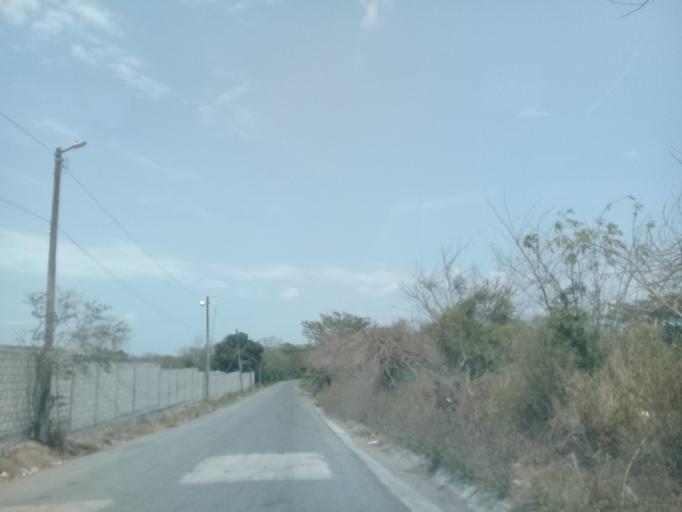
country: MX
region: Veracruz
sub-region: Veracruz
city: Delfino Victoria (Santa Fe)
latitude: 19.1697
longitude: -96.2889
